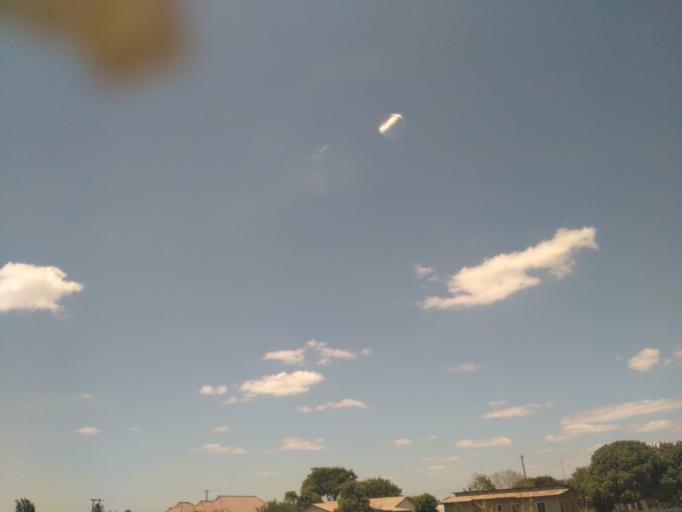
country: TZ
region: Dodoma
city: Dodoma
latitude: -6.1910
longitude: 35.7375
